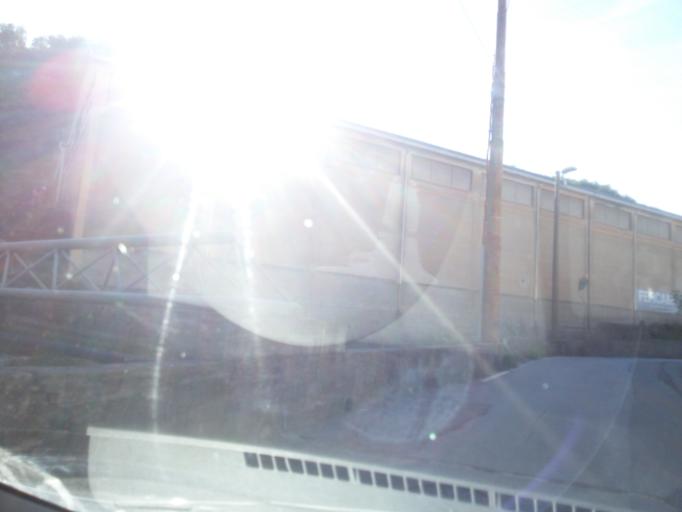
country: IT
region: Liguria
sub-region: Provincia di Genova
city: Genoa
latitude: 44.4537
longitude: 8.8900
